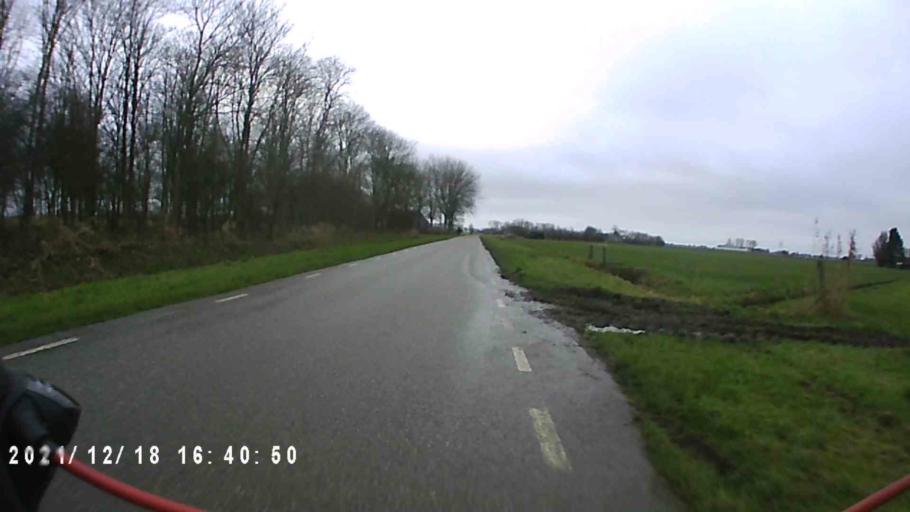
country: NL
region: Friesland
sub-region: Gemeente Dongeradeel
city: Dokkum
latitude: 53.3619
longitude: 6.0004
